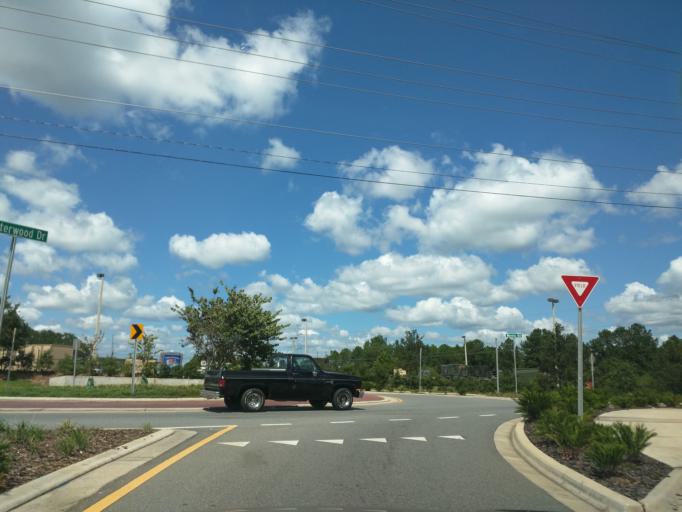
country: US
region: Florida
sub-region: Leon County
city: Tallahassee
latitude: 30.4513
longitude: -84.2239
